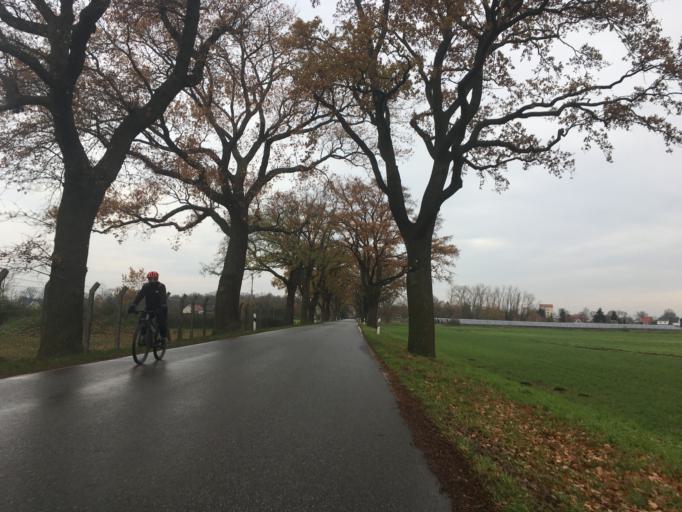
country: DE
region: Brandenburg
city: Letschin
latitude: 52.6951
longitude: 14.4042
